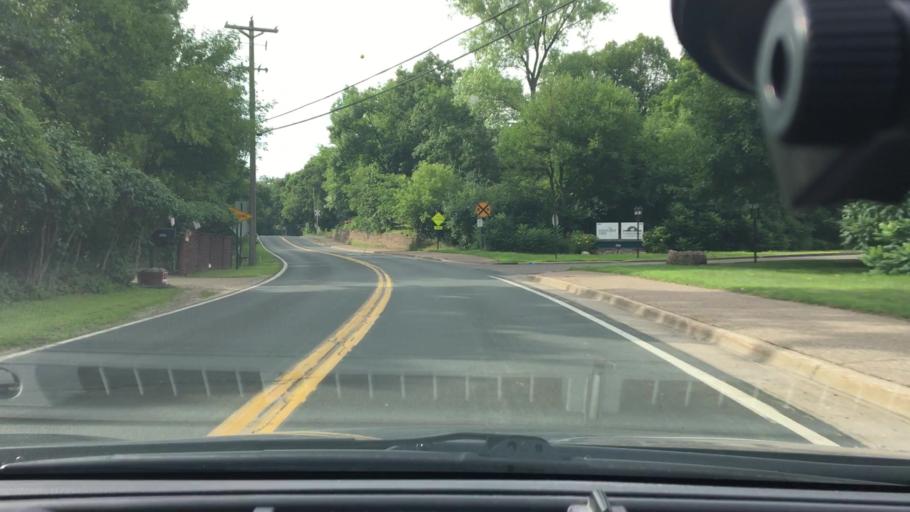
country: US
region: Minnesota
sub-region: Hennepin County
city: Plymouth
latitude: 44.9925
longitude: -93.4251
